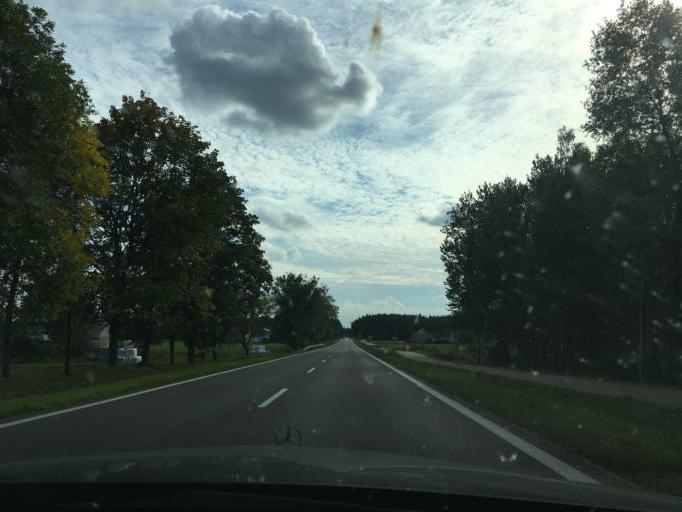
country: PL
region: Podlasie
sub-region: Powiat grajewski
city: Rajgrod
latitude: 53.7189
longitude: 22.6748
